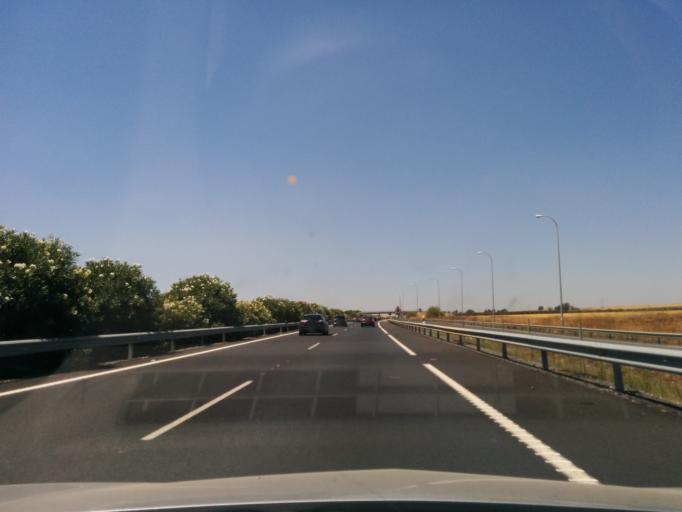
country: ES
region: Andalusia
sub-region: Provincia de Huelva
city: San Juan del Puerto
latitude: 37.3335
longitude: -6.7901
